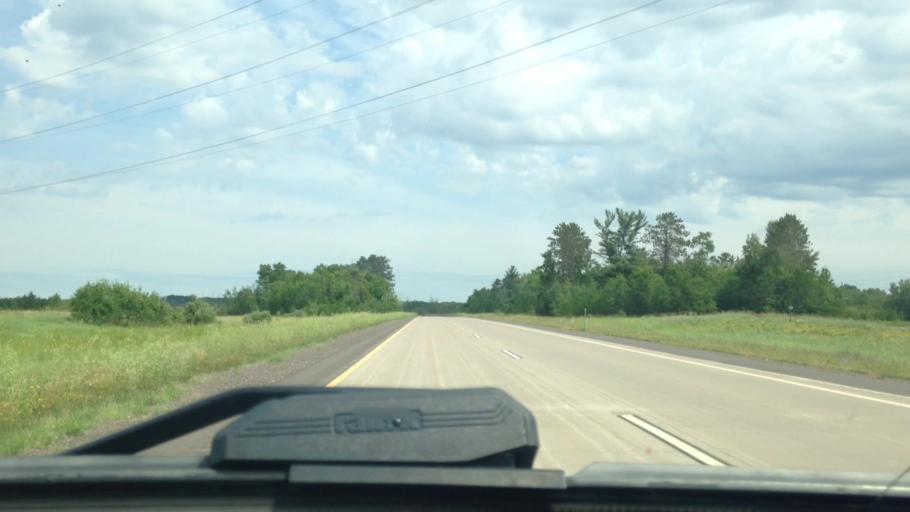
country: US
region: Wisconsin
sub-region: Douglas County
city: Lake Nebagamon
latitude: 46.2568
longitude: -91.8010
